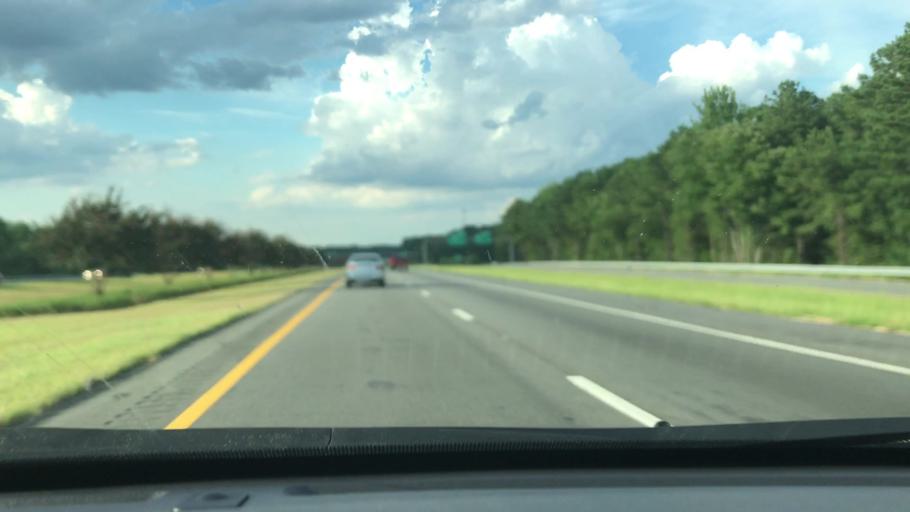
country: US
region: North Carolina
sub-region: Cumberland County
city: Vander
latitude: 35.0364
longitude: -78.8052
